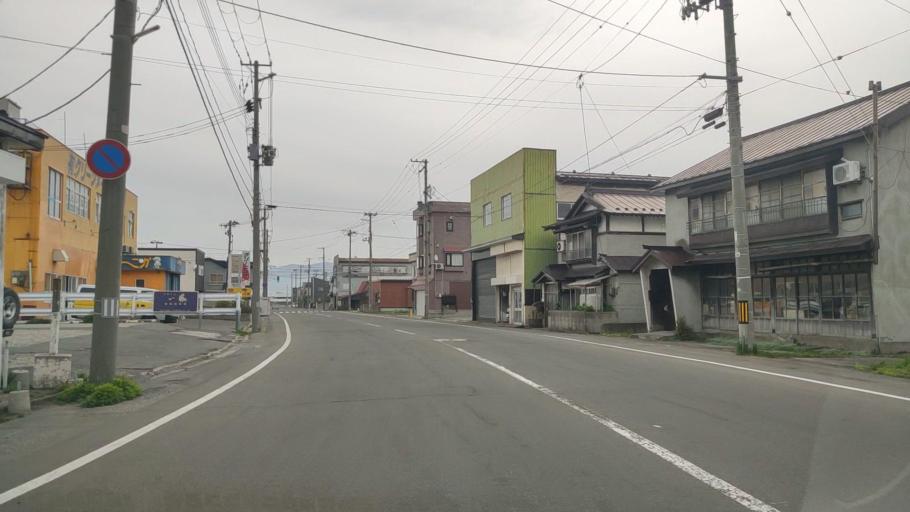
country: JP
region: Aomori
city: Aomori Shi
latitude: 40.8290
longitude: 140.7560
